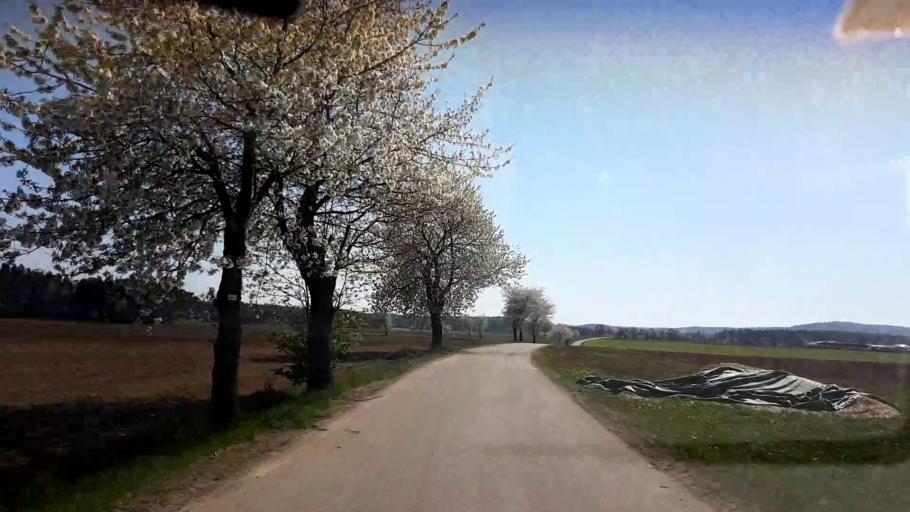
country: DE
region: Bavaria
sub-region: Upper Franconia
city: Heiligenstadt
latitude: 49.9014
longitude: 11.1748
